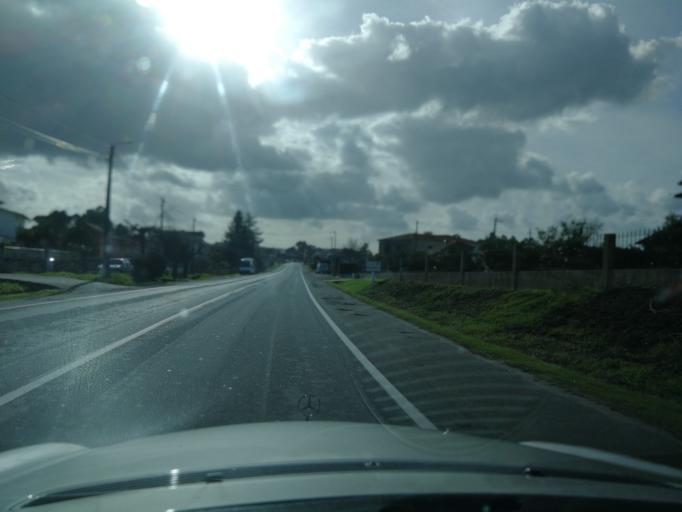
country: PT
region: Viana do Castelo
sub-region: Valenca
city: Valenza
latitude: 42.0309
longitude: -8.6304
